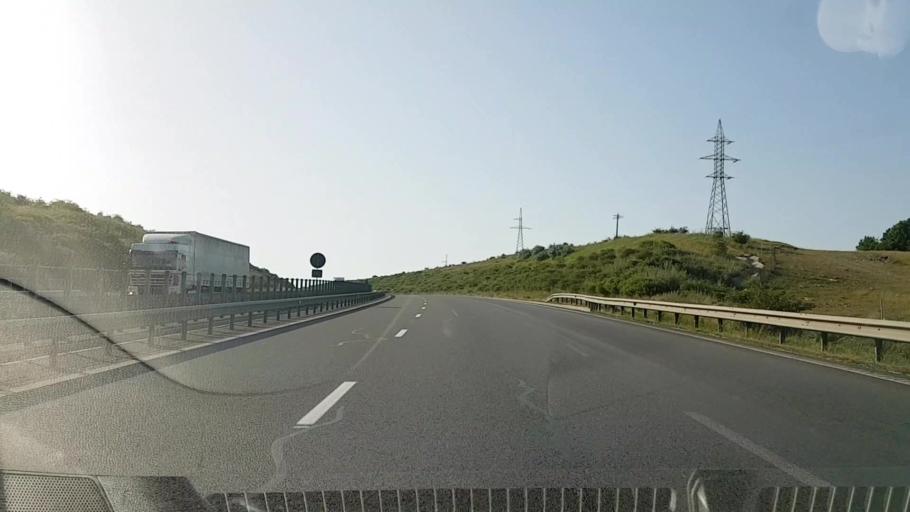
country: RO
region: Cluj
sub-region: Comuna Sandulesti
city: Sandulesti
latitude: 46.5985
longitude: 23.7085
